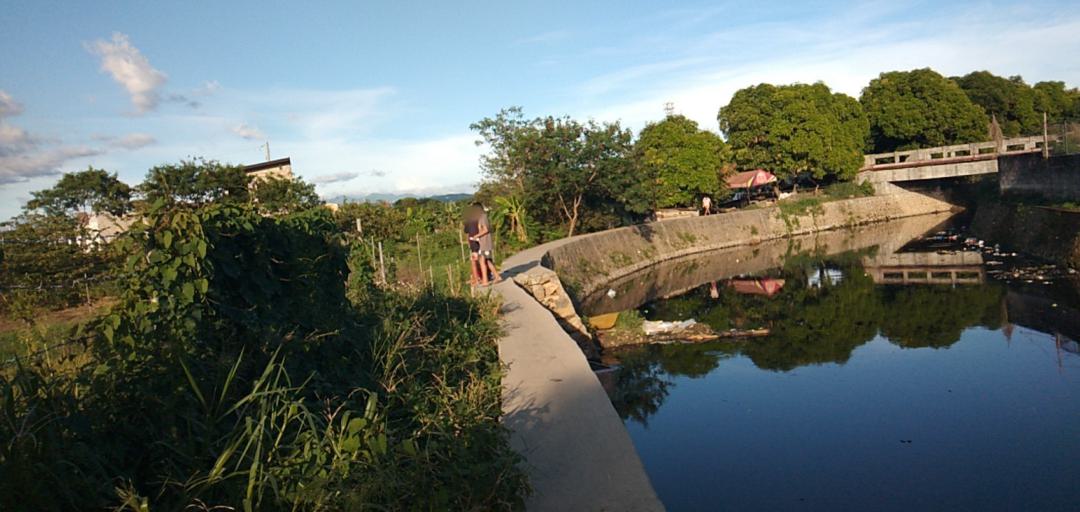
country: PH
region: Calabarzon
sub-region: Province of Rizal
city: Taytay
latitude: 14.5537
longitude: 121.1204
